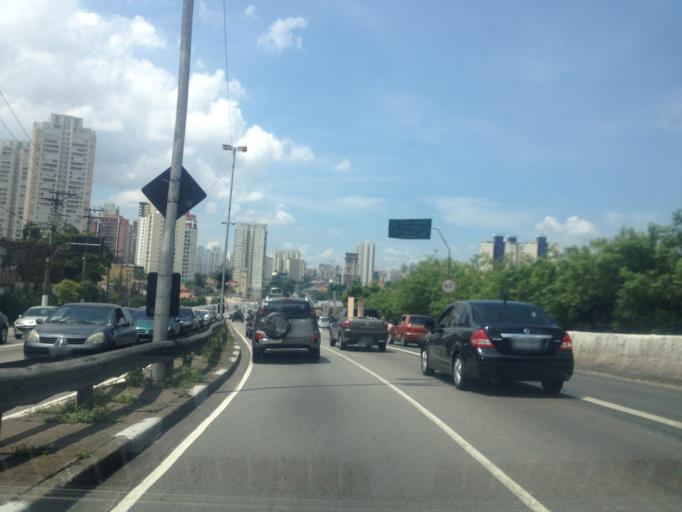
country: BR
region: Sao Paulo
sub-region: Diadema
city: Diadema
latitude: -23.6405
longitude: -46.6738
